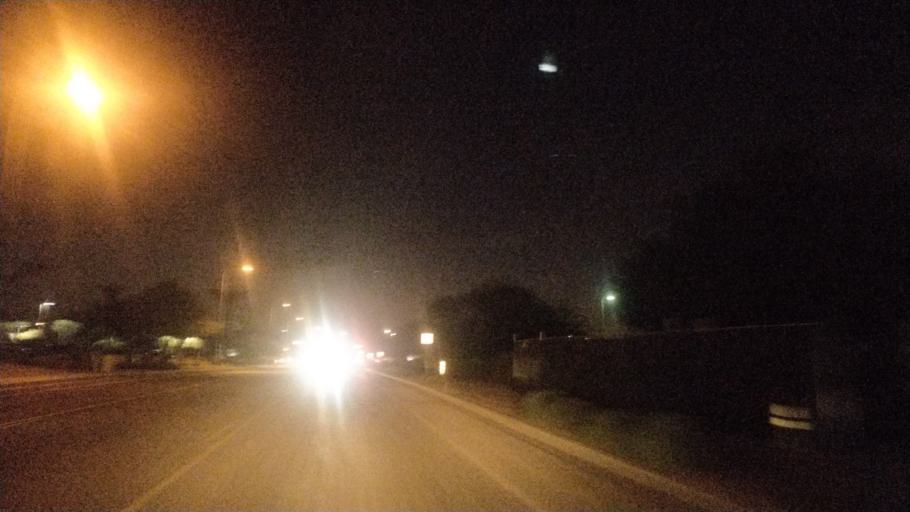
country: US
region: Arizona
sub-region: Maricopa County
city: Chandler
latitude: 33.2838
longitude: -111.8562
